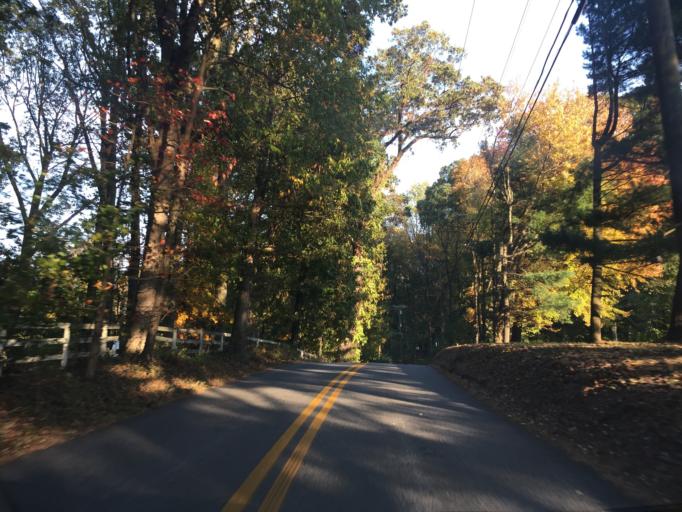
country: US
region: Maryland
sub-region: Baltimore County
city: Hampton
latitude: 39.4873
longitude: -76.5523
